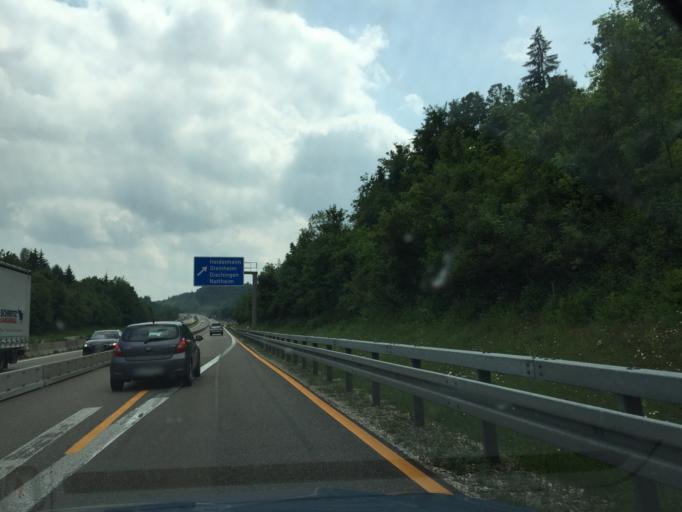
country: DE
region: Baden-Wuerttemberg
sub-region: Regierungsbezirk Stuttgart
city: Nattheim
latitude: 48.6953
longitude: 10.2147
